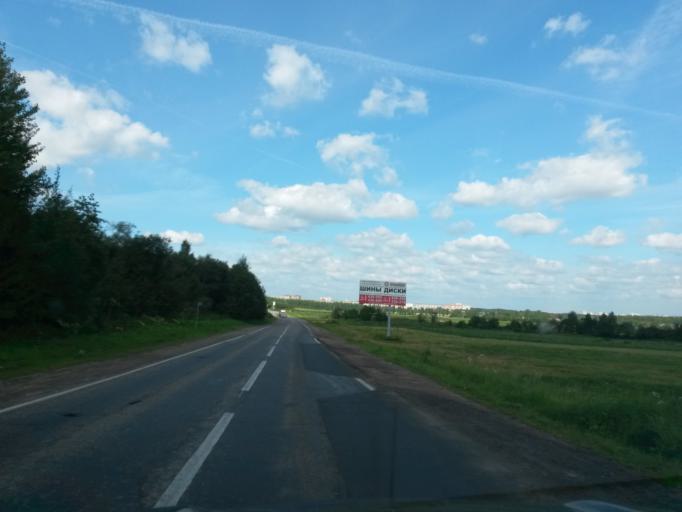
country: RU
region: Jaroslavl
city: Yaroslavl
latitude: 57.5465
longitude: 39.8618
